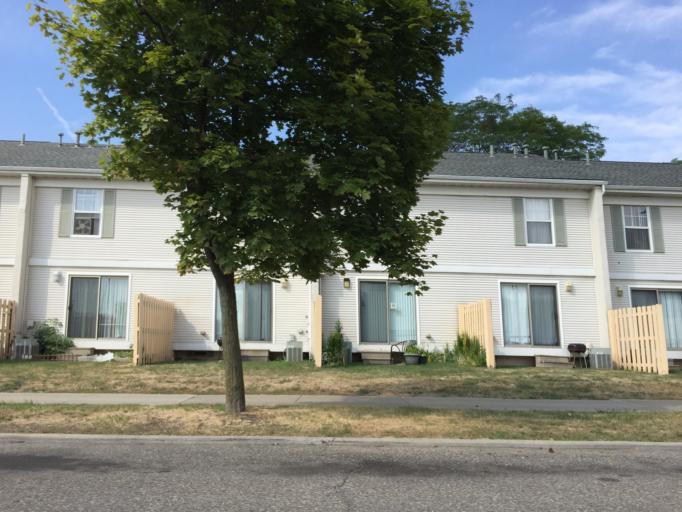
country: US
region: Michigan
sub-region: Wayne County
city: Detroit
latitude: 42.3410
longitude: -83.0247
